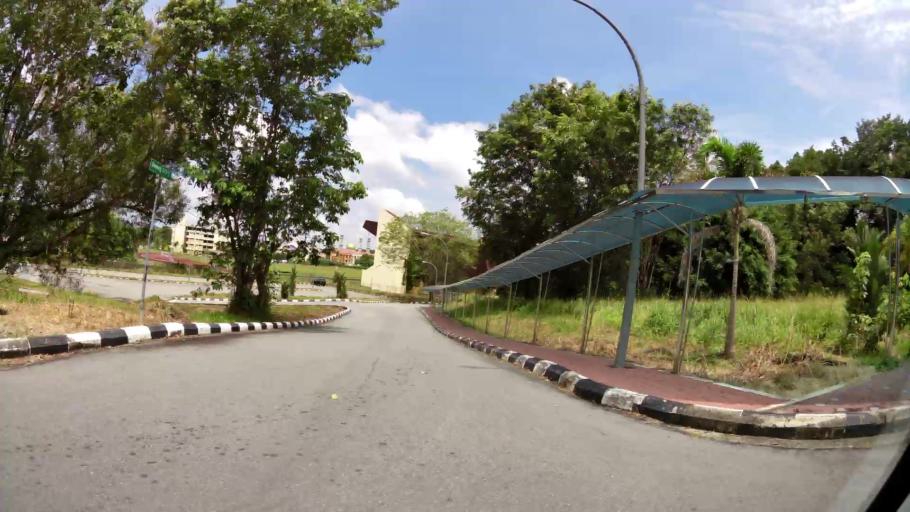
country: BN
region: Brunei and Muara
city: Bandar Seri Begawan
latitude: 4.9034
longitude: 114.9148
